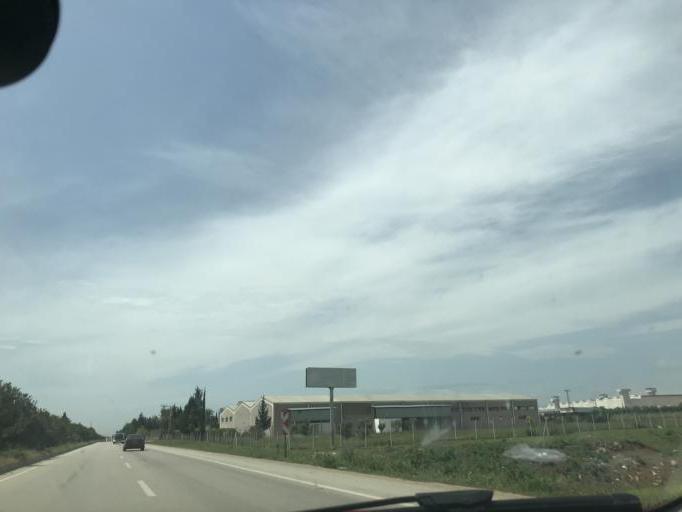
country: TR
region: Adana
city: Yakapinar
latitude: 36.9715
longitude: 35.5208
